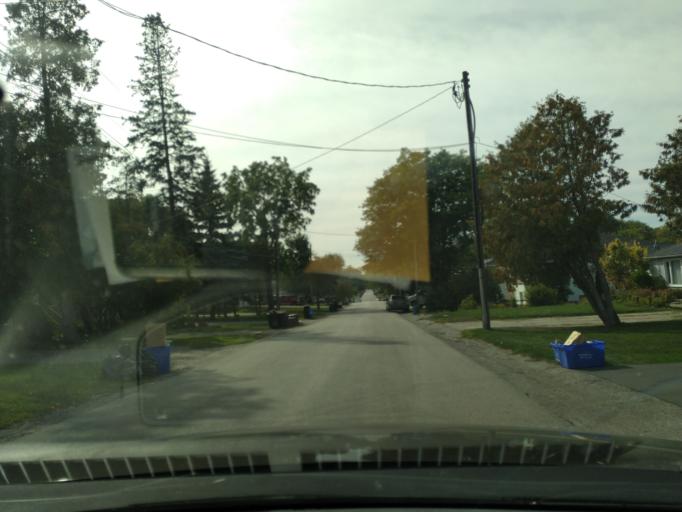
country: CA
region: Ontario
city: Keswick
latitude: 44.2168
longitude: -79.4654
